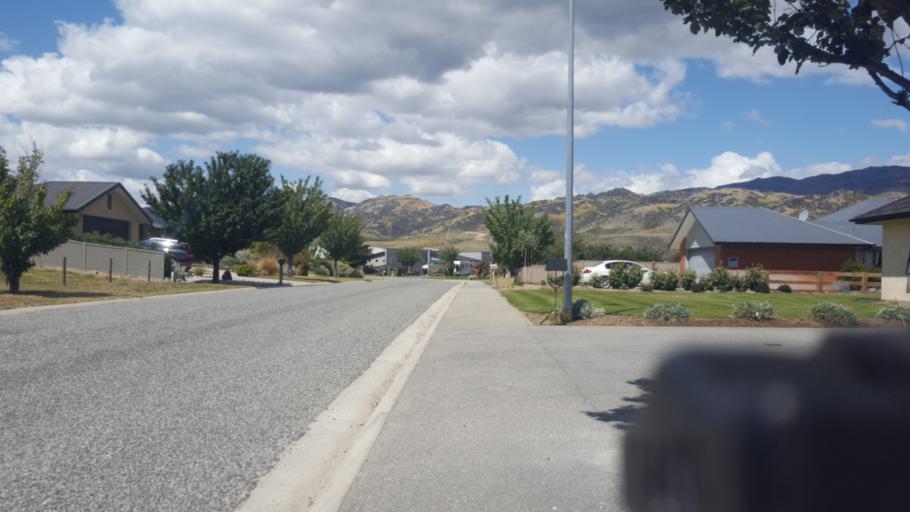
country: NZ
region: Otago
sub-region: Queenstown-Lakes District
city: Wanaka
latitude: -44.9726
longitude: 169.2468
